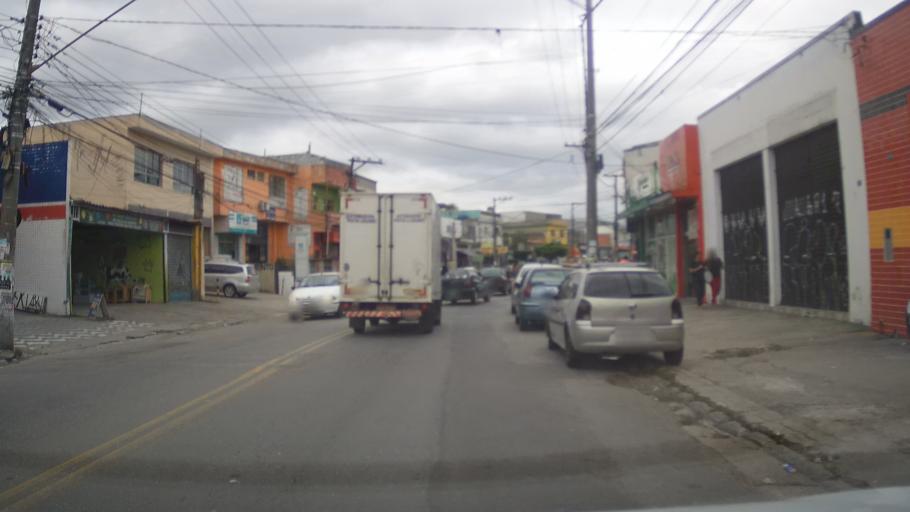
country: BR
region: Sao Paulo
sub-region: Itaquaquecetuba
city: Itaquaquecetuba
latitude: -23.4265
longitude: -46.4322
